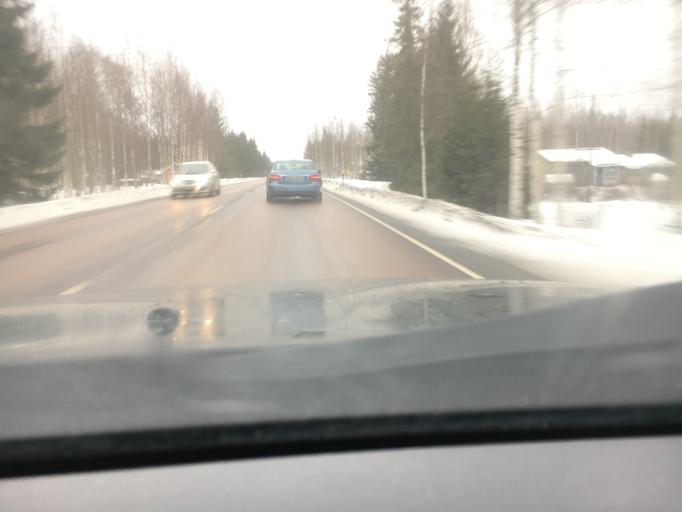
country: FI
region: Central Finland
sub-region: Joutsa
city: Leivonmaeki
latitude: 61.8850
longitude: 26.1127
